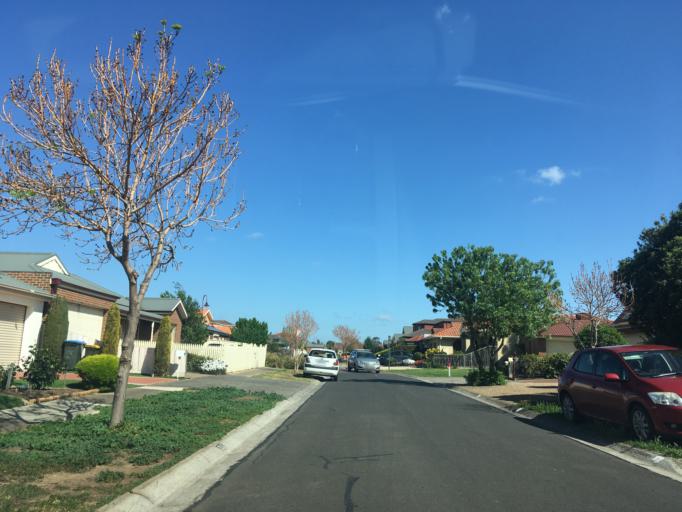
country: AU
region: Victoria
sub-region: Wyndham
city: Hoppers Crossing
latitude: -37.8765
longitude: 144.7059
